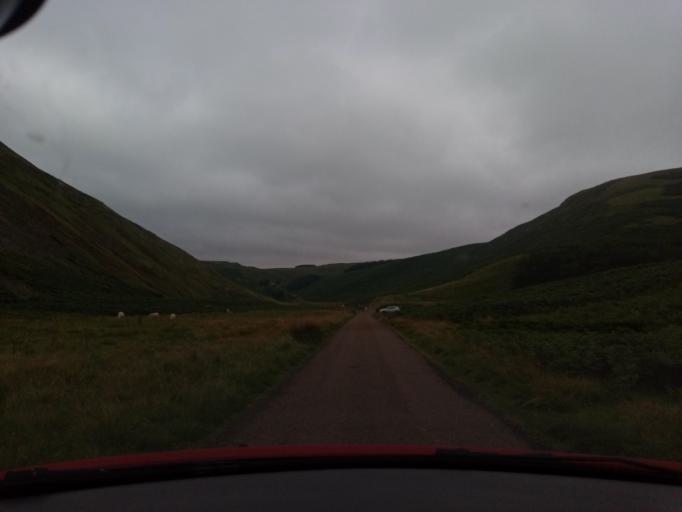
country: GB
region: England
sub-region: Northumberland
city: Rochester
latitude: 55.3780
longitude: -2.2155
